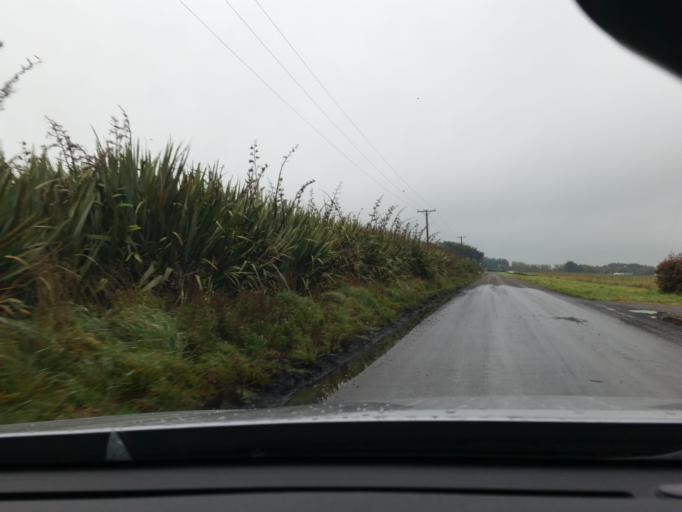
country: NZ
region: Southland
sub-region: Invercargill City
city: Invercargill
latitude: -46.3041
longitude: 168.3033
